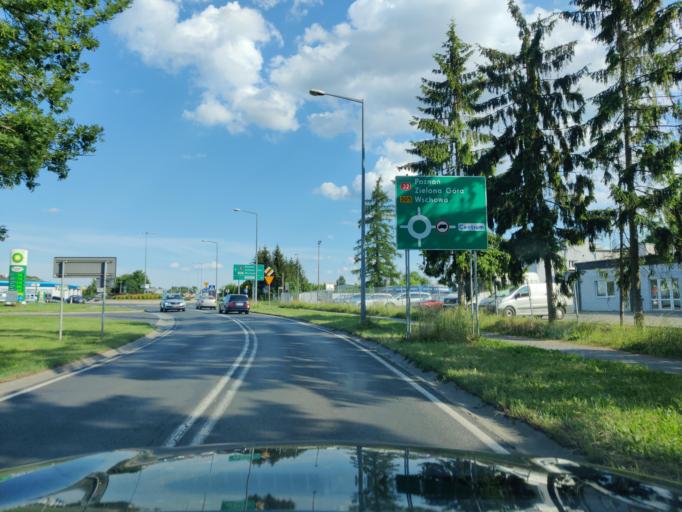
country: PL
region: Greater Poland Voivodeship
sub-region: Powiat wolsztynski
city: Wolsztyn
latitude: 52.1246
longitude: 16.1235
